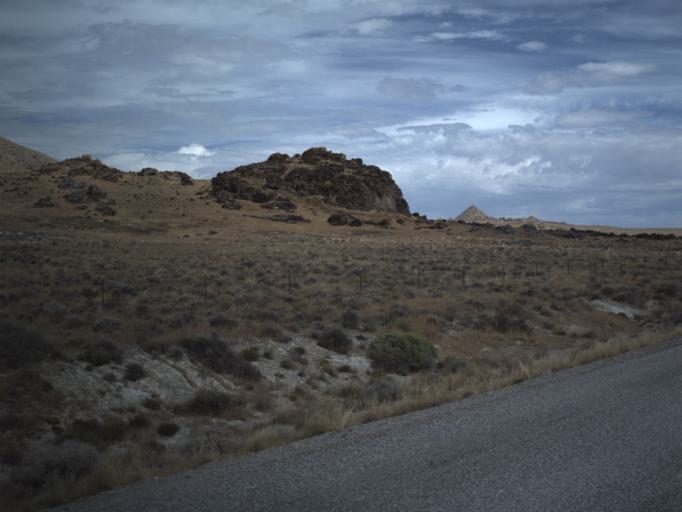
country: US
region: Utah
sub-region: Tooele County
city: Wendover
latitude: 41.4612
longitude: -113.6511
